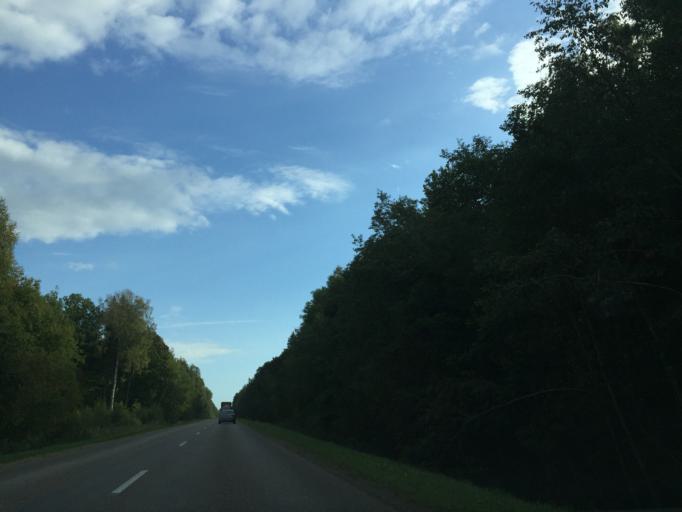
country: LV
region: Limbazu Rajons
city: Limbazi
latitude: 57.5169
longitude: 24.5299
